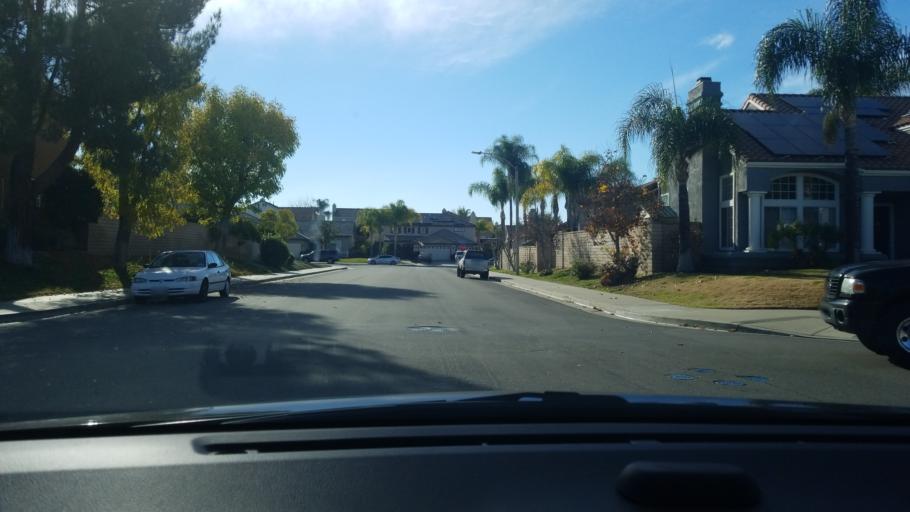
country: US
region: California
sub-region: Riverside County
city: Murrieta
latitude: 33.5711
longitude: -117.1964
